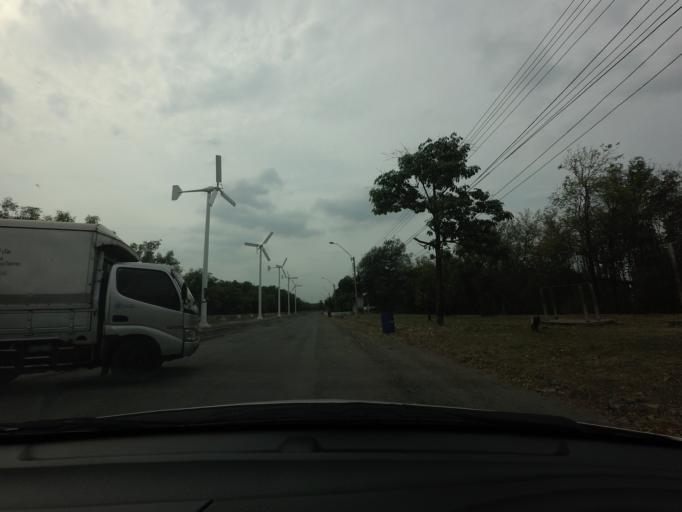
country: TH
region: Samut Prakan
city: Samut Prakan
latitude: 13.5175
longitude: 100.6537
